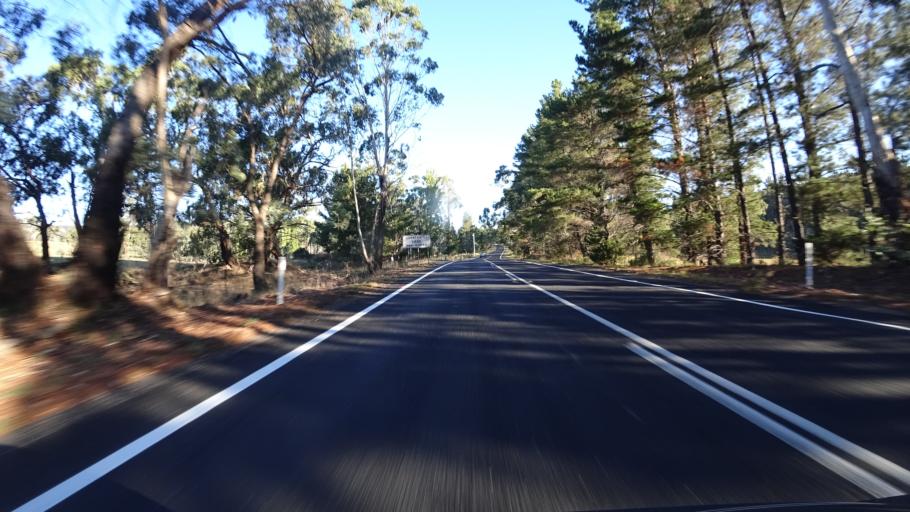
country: AU
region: New South Wales
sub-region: Lithgow
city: Portland
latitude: -33.3141
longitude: 150.0363
